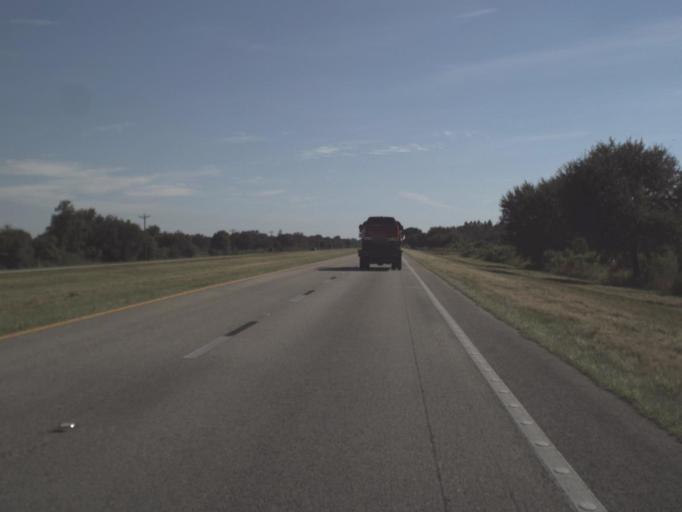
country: US
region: Florida
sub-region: Hendry County
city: Port LaBelle
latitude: 26.9980
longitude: -81.3288
